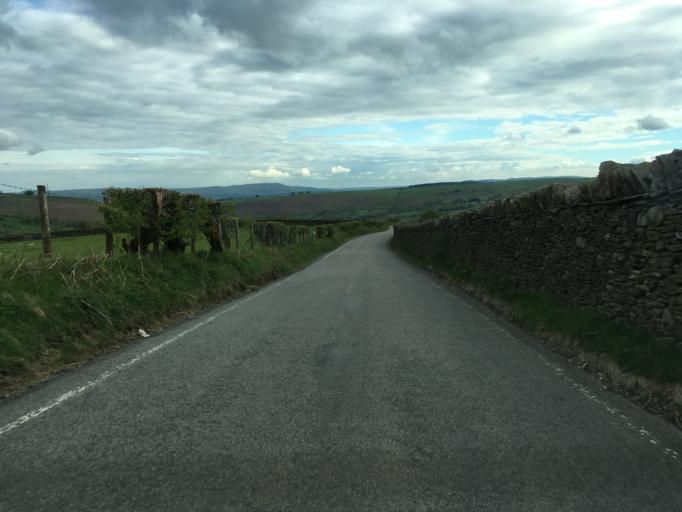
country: GB
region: Wales
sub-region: Merthyr Tydfil County Borough
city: Treharris
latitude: 51.7122
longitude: -3.3094
